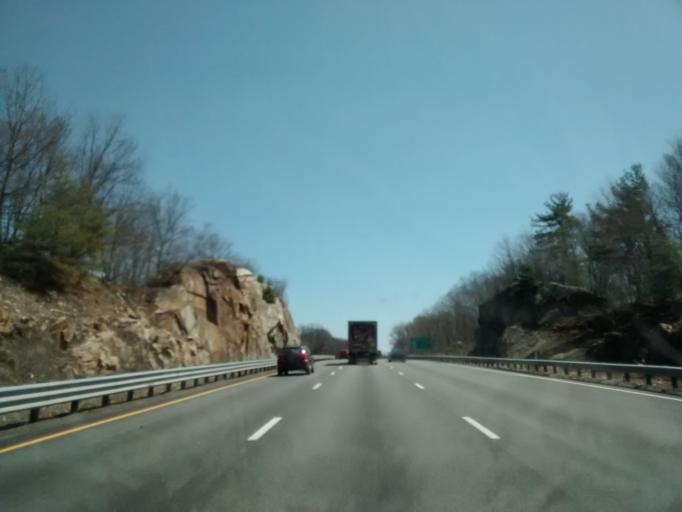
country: US
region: Massachusetts
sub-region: Worcester County
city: Milford
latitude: 42.1633
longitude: -71.5016
